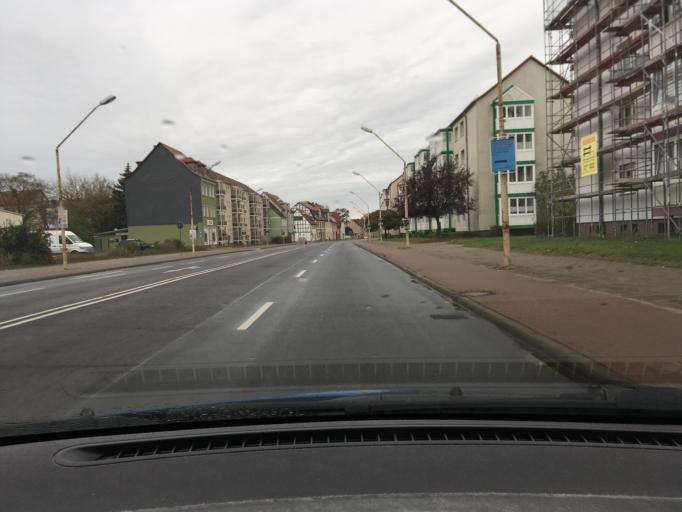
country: DE
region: Saxony-Anhalt
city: Zerbst
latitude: 51.9669
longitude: 12.0840
